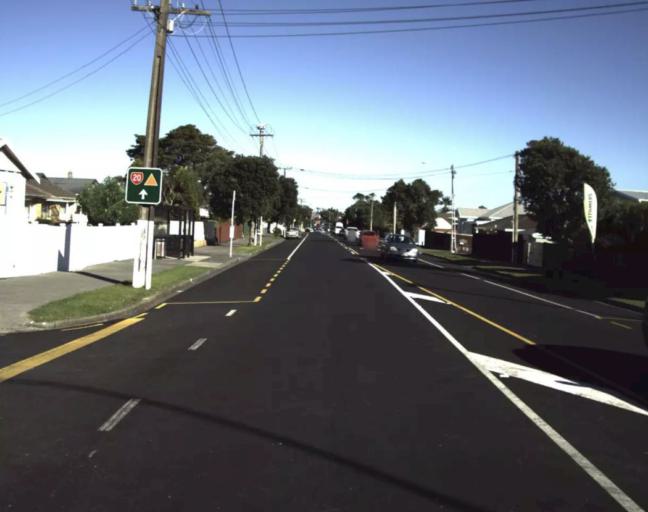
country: NZ
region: Auckland
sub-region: Auckland
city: Rosebank
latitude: -36.8911
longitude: 174.7007
